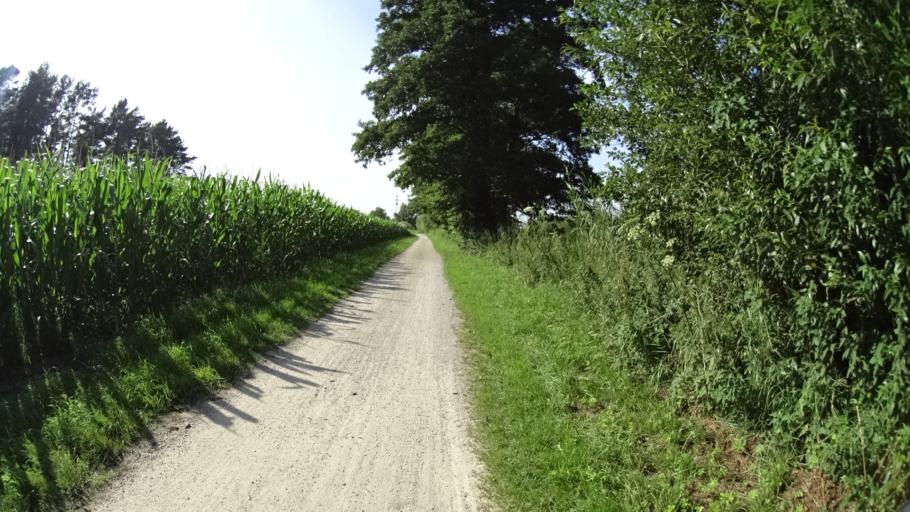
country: DE
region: Lower Saxony
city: Adendorf
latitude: 53.2784
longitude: 10.4143
